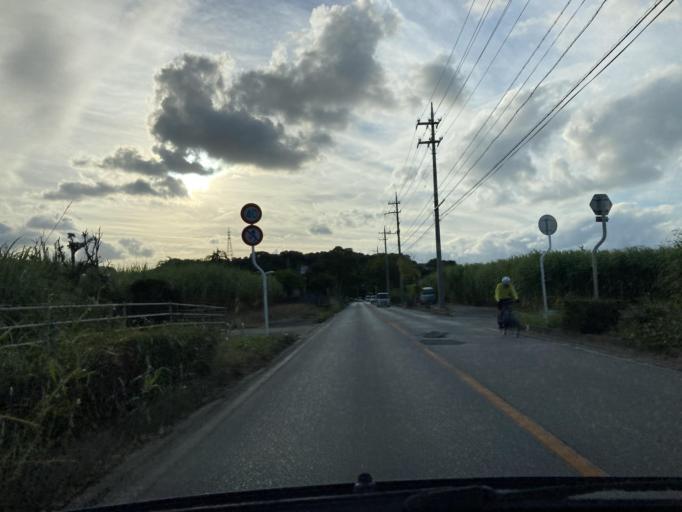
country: JP
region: Okinawa
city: Itoman
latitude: 26.1347
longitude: 127.7016
